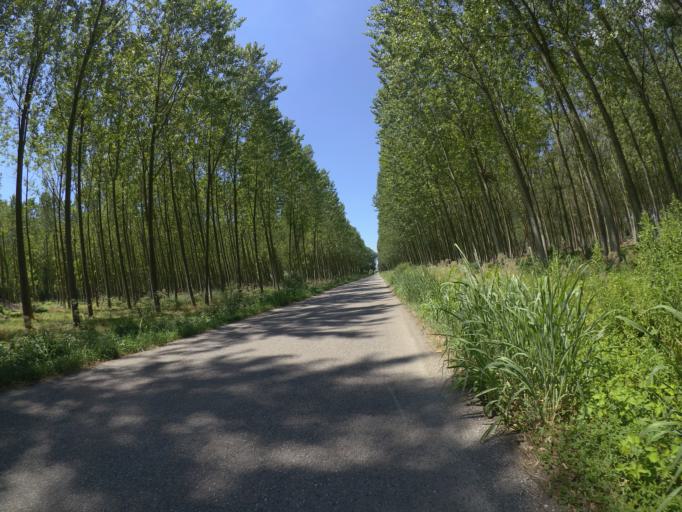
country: IT
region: Friuli Venezia Giulia
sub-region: Provincia di Udine
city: Rivignano
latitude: 45.9031
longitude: 13.0403
